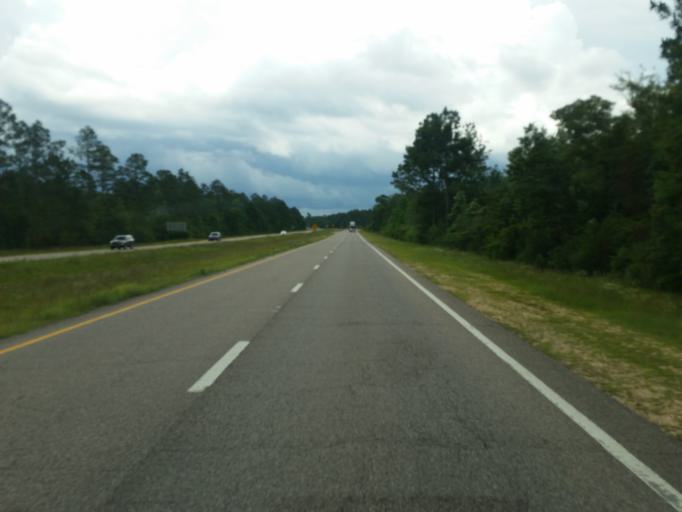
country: US
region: Mississippi
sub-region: George County
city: Lucedale
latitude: 30.8715
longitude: -88.4288
